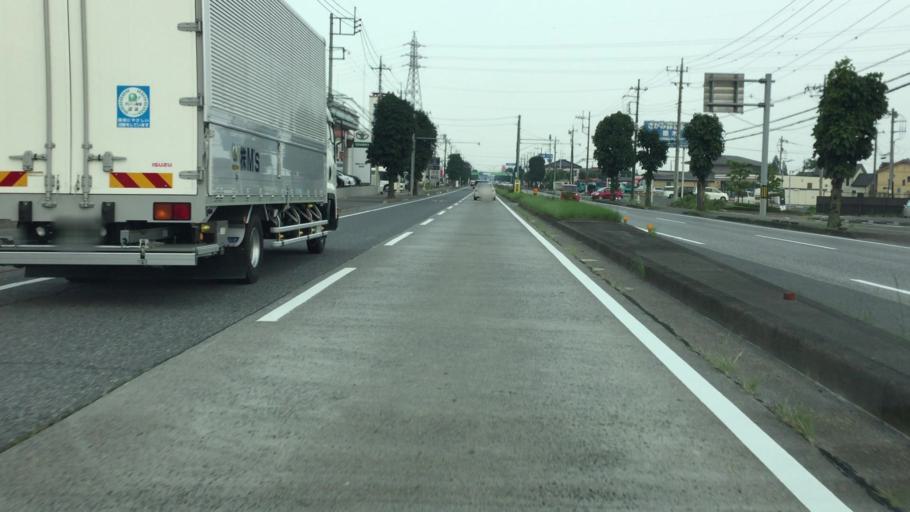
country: JP
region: Tochigi
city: Tochigi
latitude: 36.4012
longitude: 139.7146
